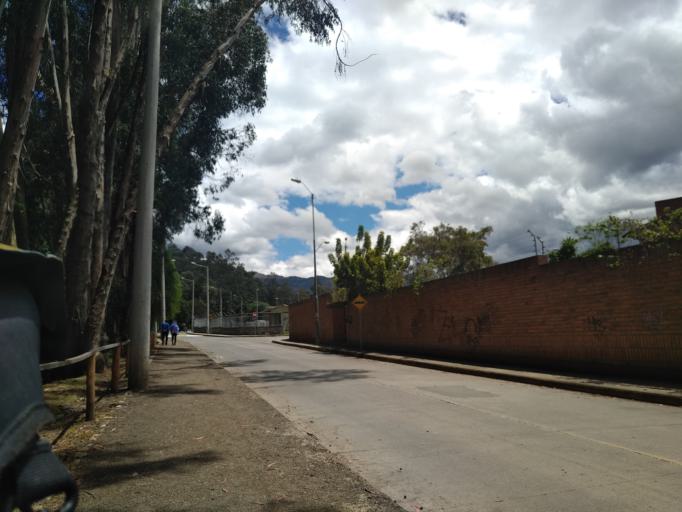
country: EC
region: Azuay
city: Cuenca
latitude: -2.8901
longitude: -79.0335
